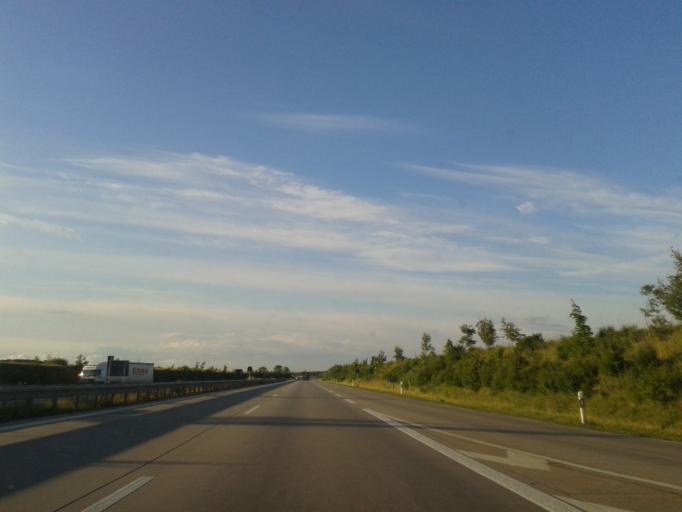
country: DE
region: Saxony
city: Grossposna
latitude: 51.2771
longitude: 12.4924
